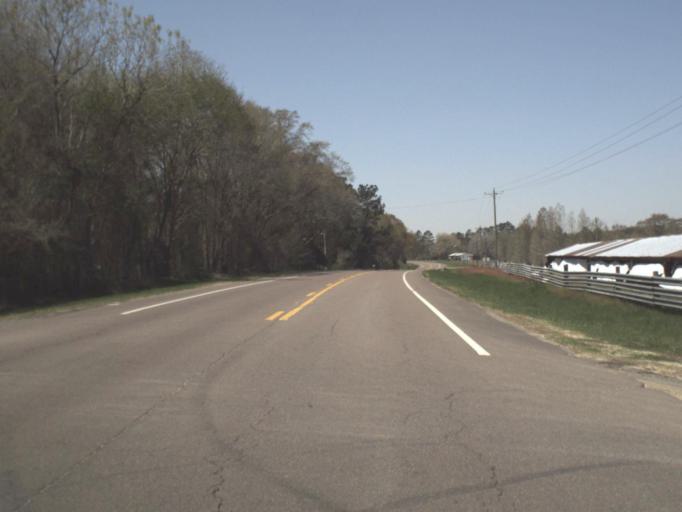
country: US
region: Alabama
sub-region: Geneva County
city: Hartford
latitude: 30.9596
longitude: -85.6931
